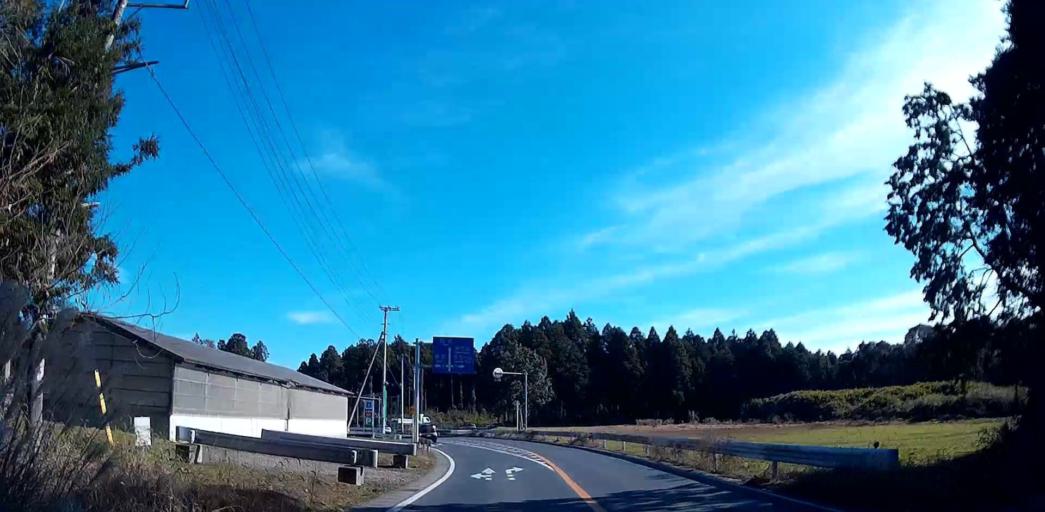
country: JP
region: Chiba
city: Yokaichiba
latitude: 35.7592
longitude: 140.4549
